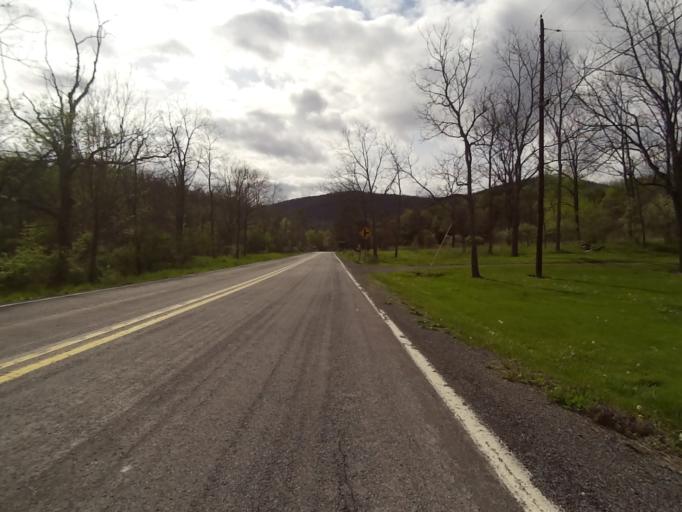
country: US
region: Pennsylvania
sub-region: Centre County
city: Park Forest Village
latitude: 40.8852
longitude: -77.9691
